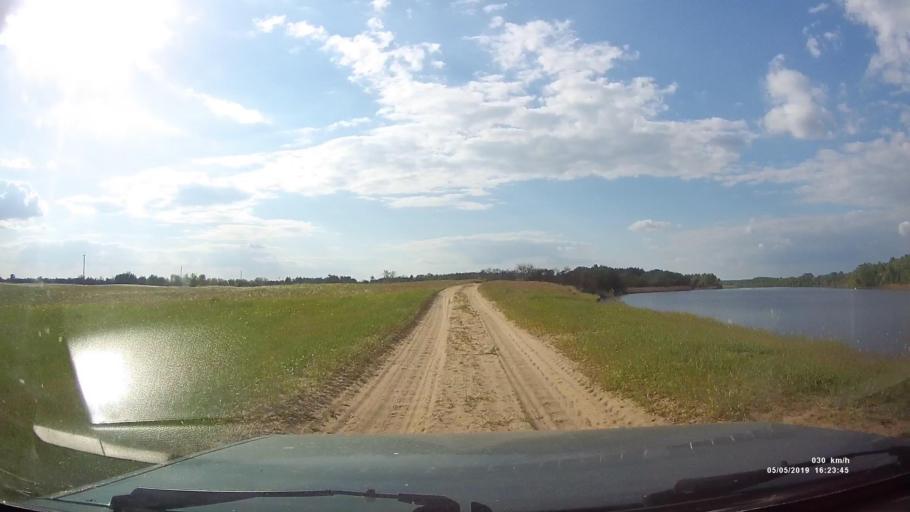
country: RU
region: Rostov
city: Konstantinovsk
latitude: 47.7574
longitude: 41.0293
